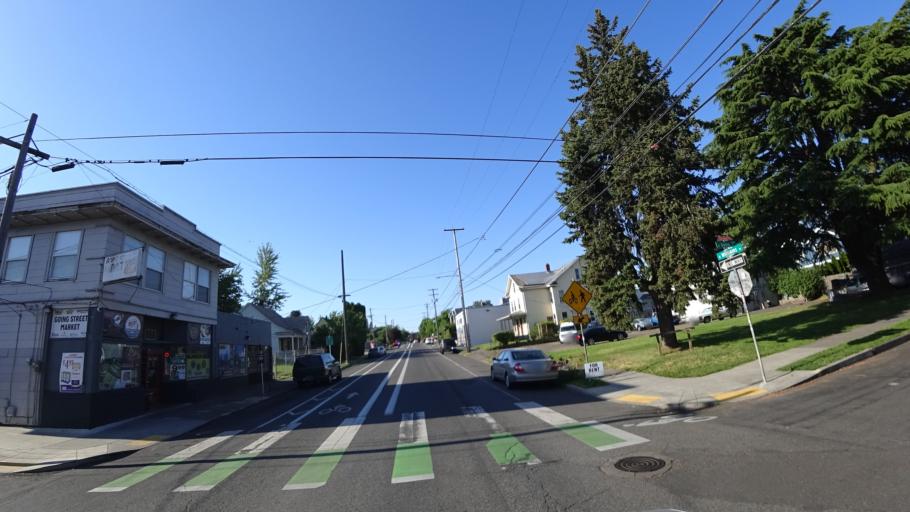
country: US
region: Oregon
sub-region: Multnomah County
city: Portland
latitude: 45.5564
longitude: -122.6667
